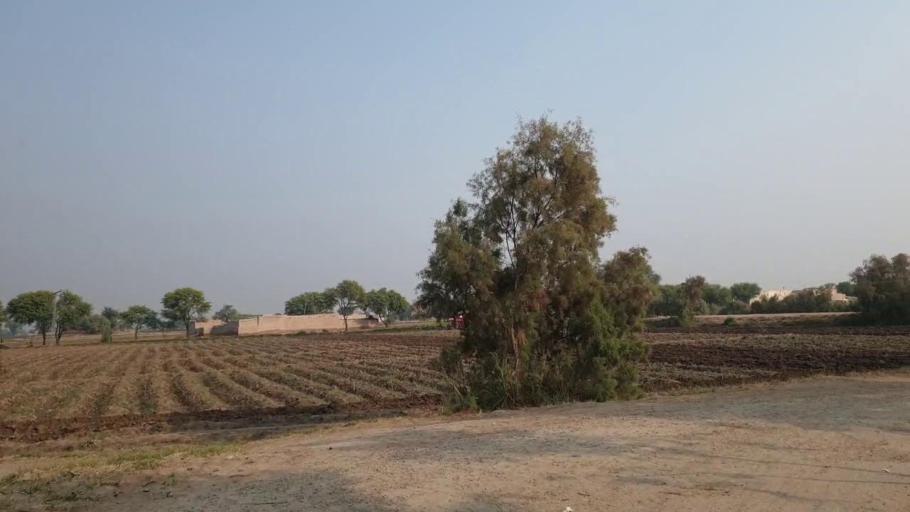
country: PK
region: Sindh
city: Bhan
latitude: 26.4584
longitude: 67.7277
